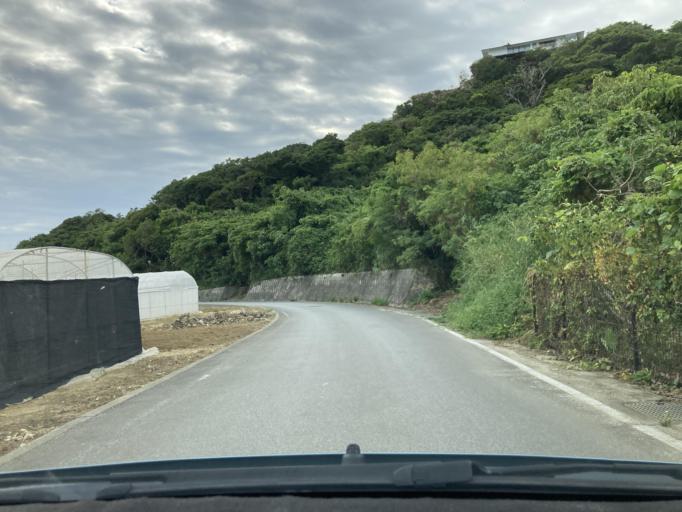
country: JP
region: Okinawa
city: Tomigusuku
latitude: 26.1370
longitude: 127.7932
